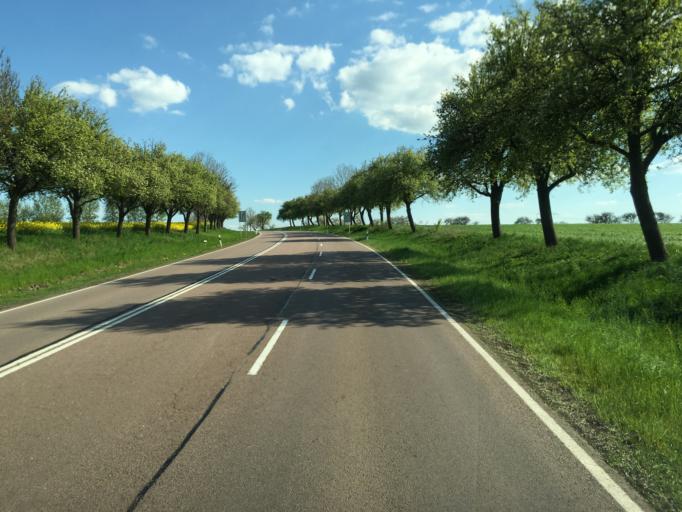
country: DE
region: Saxony
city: Dobeln
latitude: 51.1117
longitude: 13.0932
